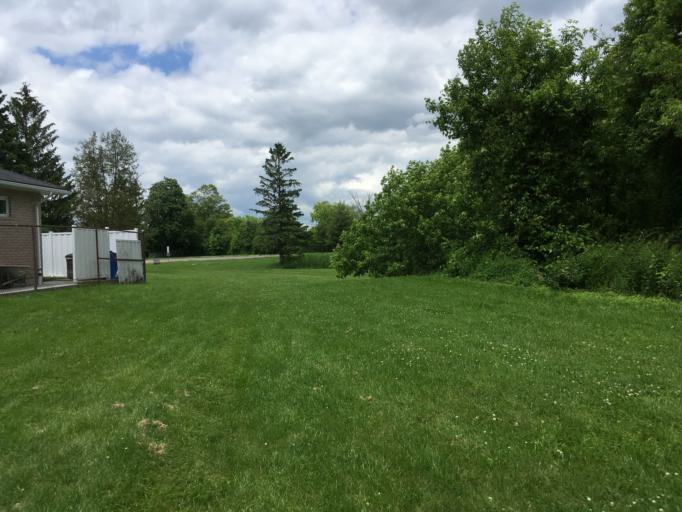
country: CA
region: Ontario
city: Oshawa
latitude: 43.8751
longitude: -78.8557
